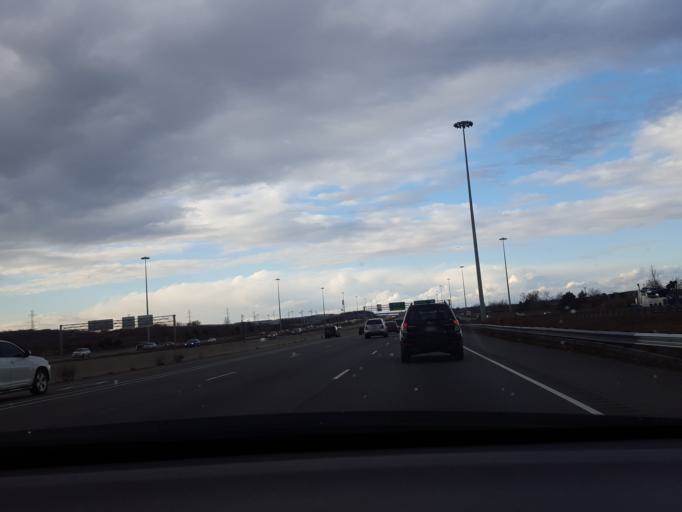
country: CA
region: Ontario
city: Mississauga
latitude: 43.6220
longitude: -79.6364
